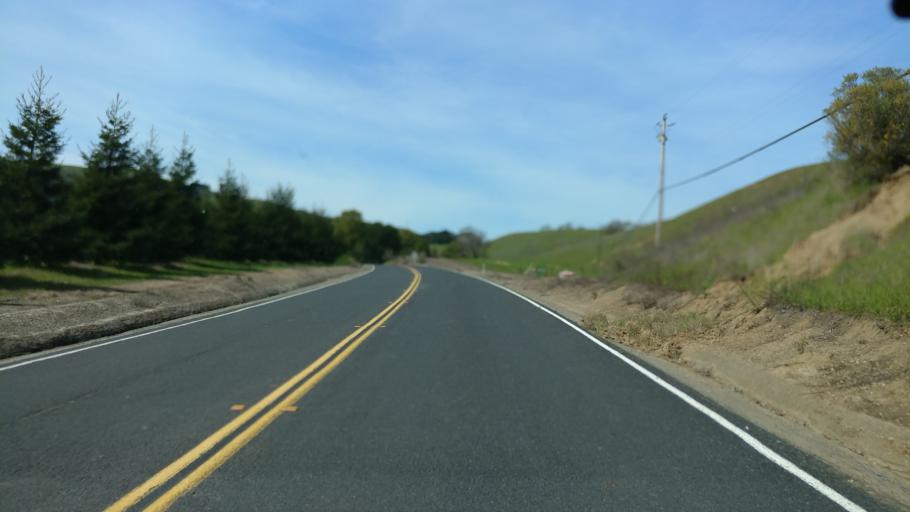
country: US
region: California
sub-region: Contra Costa County
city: Danville
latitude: 37.7947
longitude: -122.0186
